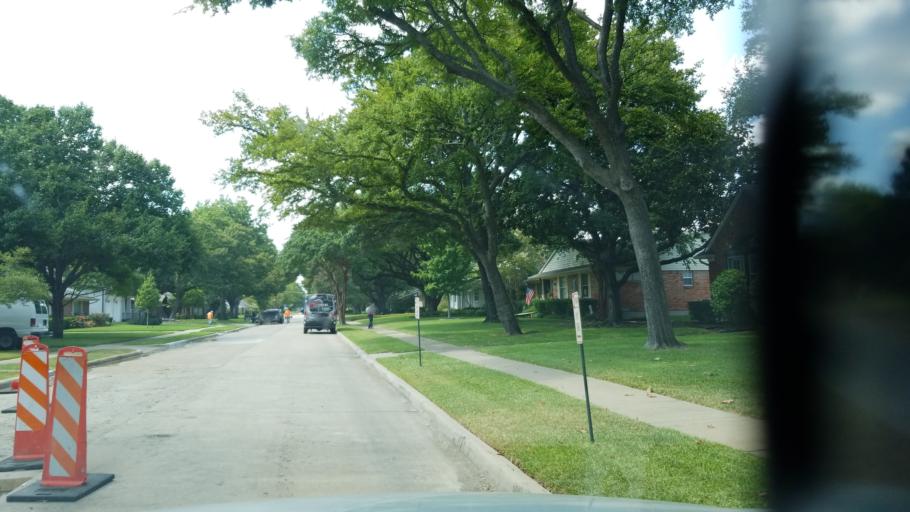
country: US
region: Texas
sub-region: Dallas County
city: Richardson
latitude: 32.9690
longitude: -96.7611
